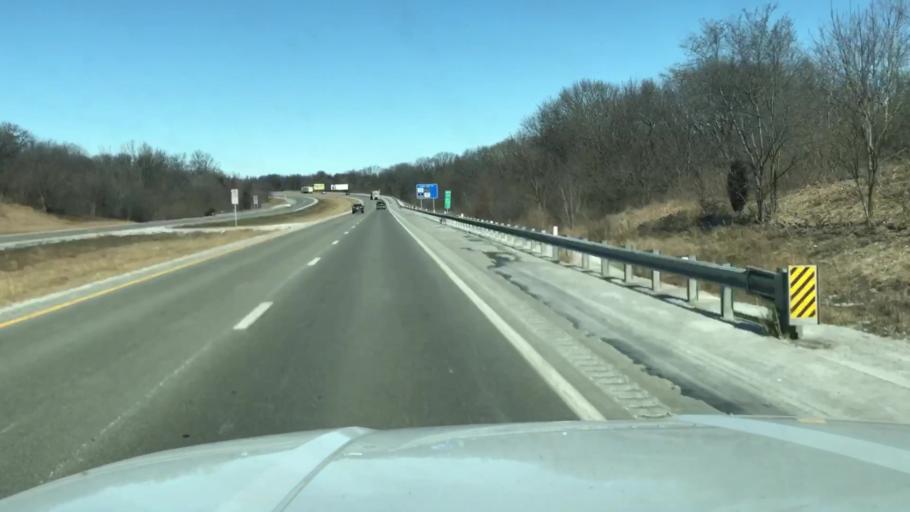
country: US
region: Missouri
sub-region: Andrew County
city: Country Club Village
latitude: 39.8485
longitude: -94.8051
